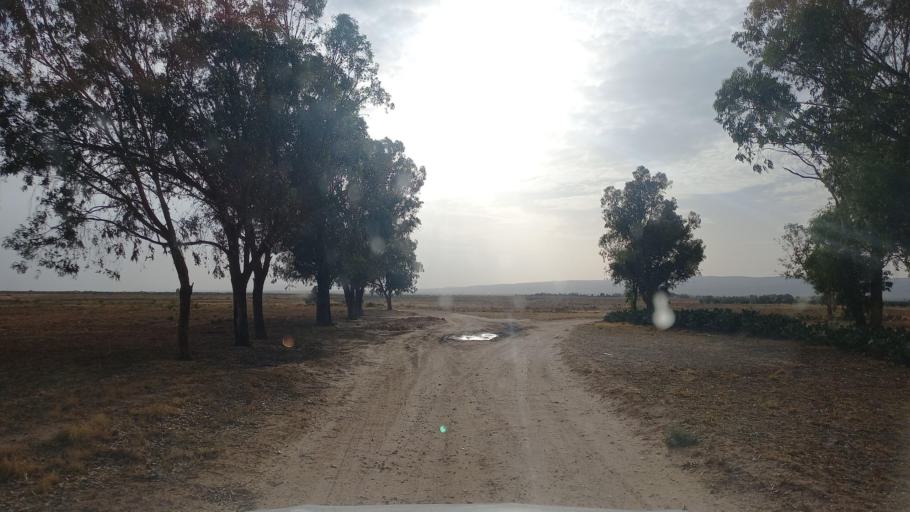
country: TN
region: Al Qasrayn
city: Kasserine
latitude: 35.2928
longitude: 9.0522
